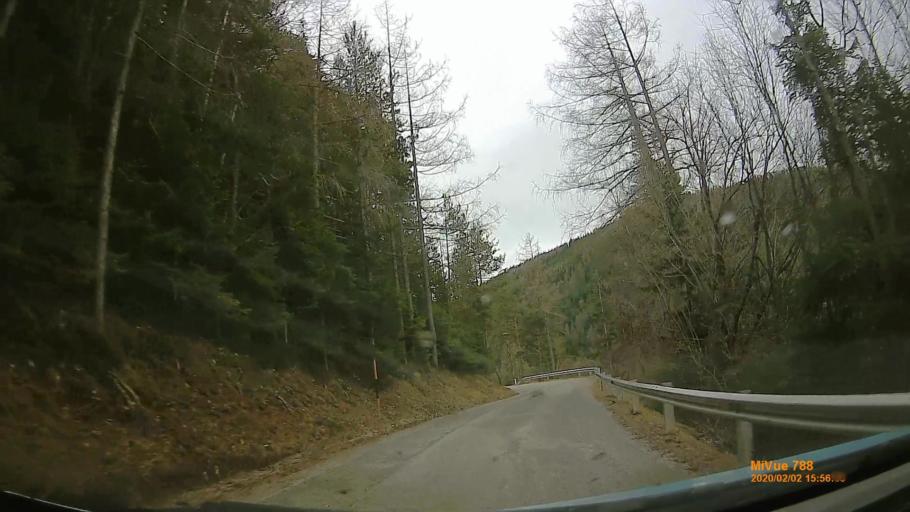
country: AT
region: Lower Austria
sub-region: Politischer Bezirk Neunkirchen
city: Semmering
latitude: 47.6680
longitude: 15.7838
